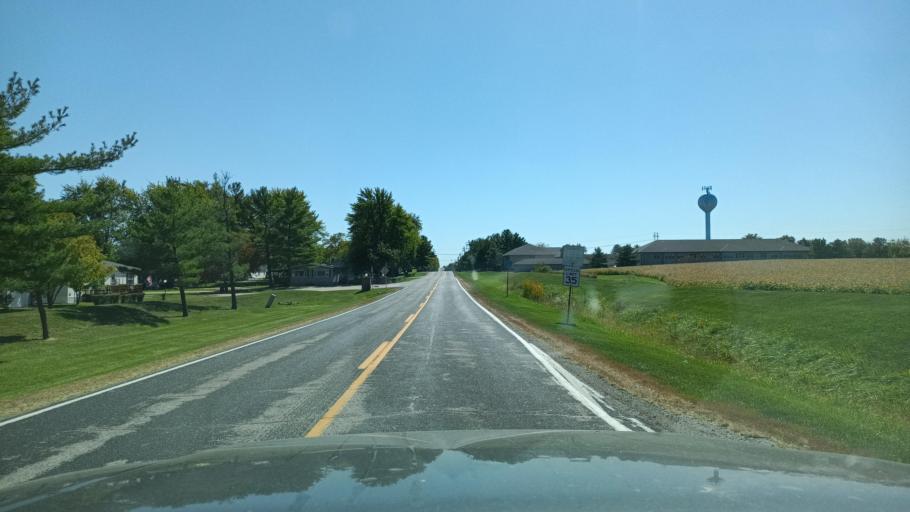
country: US
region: Illinois
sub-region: Champaign County
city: Lake of the Woods
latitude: 40.2077
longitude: -88.3653
